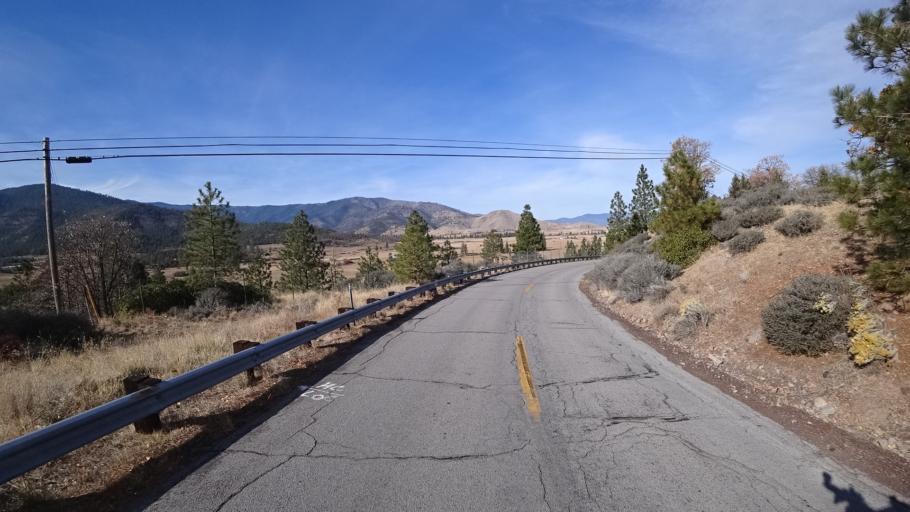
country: US
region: California
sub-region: Siskiyou County
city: Weed
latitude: 41.4326
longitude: -122.4288
